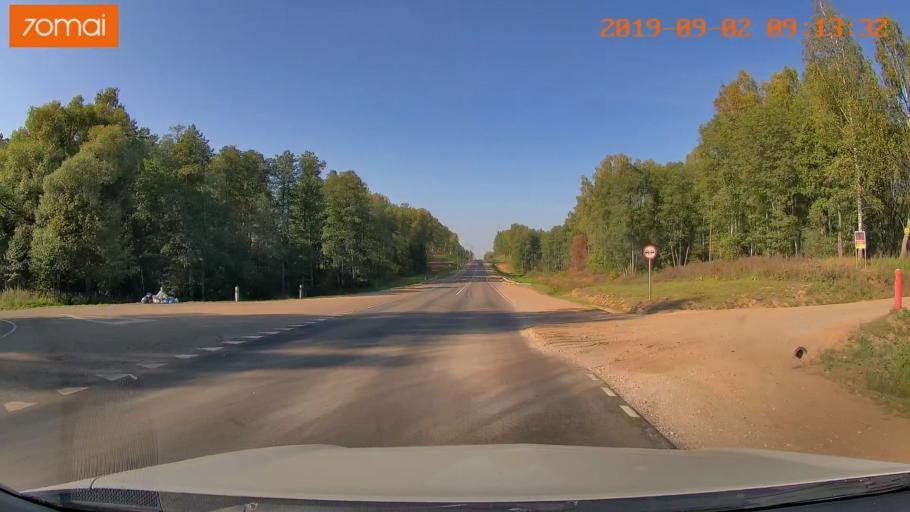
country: RU
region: Kaluga
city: Nikola-Lenivets
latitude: 54.8524
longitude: 35.5322
